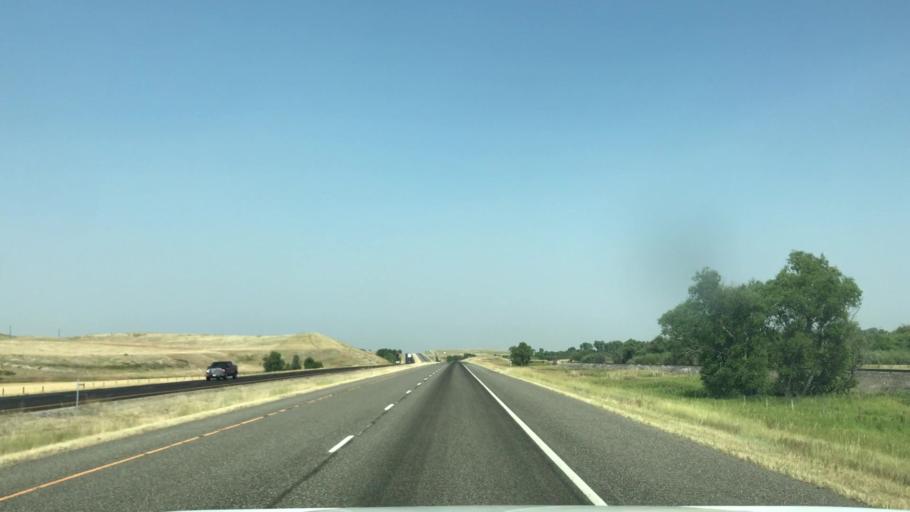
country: US
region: Montana
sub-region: Cascade County
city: Sun Prairie
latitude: 47.2379
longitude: -111.7372
